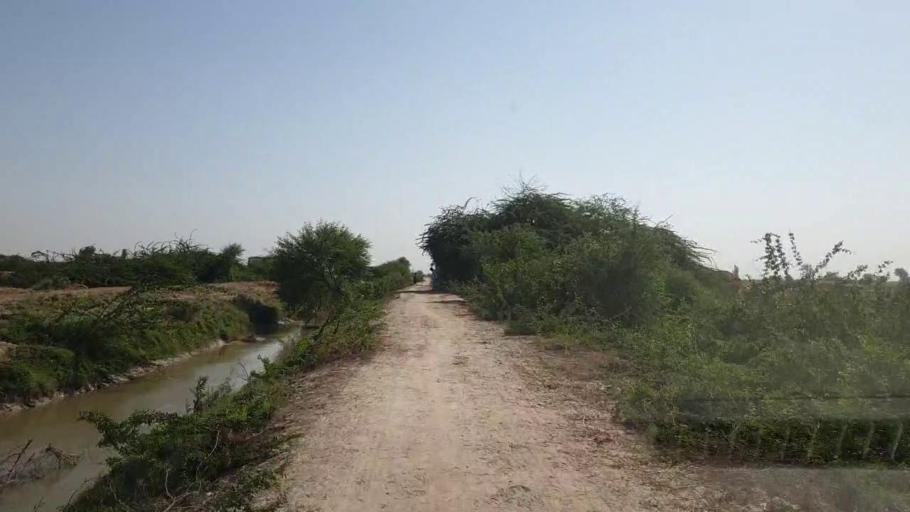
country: PK
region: Sindh
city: Kadhan
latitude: 24.6168
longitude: 68.9973
